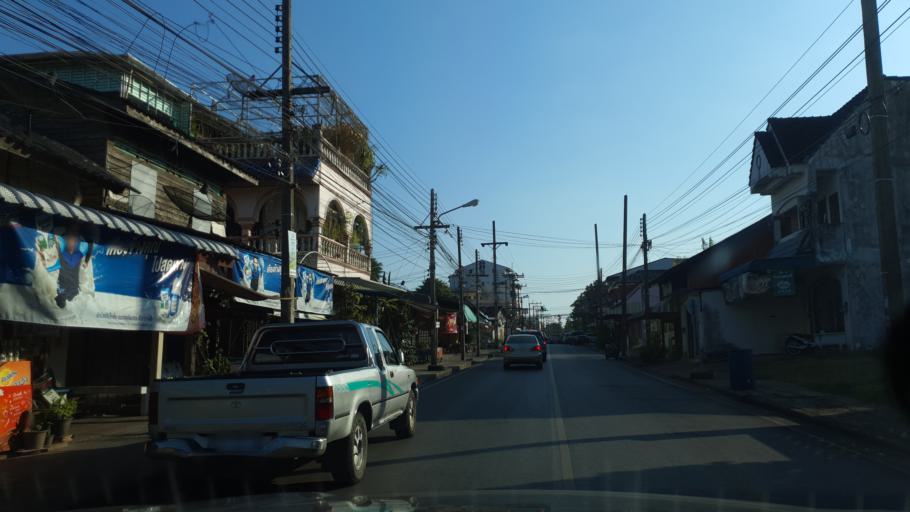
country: TH
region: Krabi
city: Krabi
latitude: 8.1028
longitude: 98.9114
